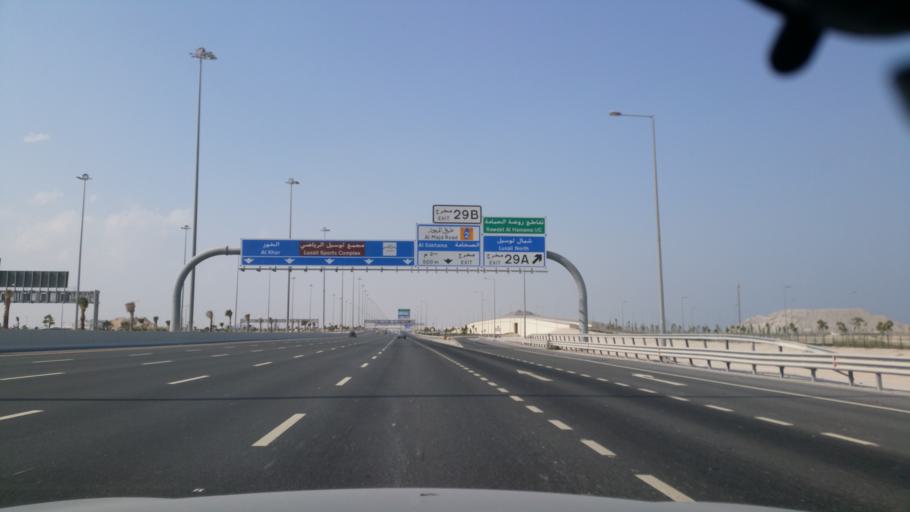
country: QA
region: Baladiyat Umm Salal
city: Umm Salal Muhammad
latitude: 25.4439
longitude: 51.4814
